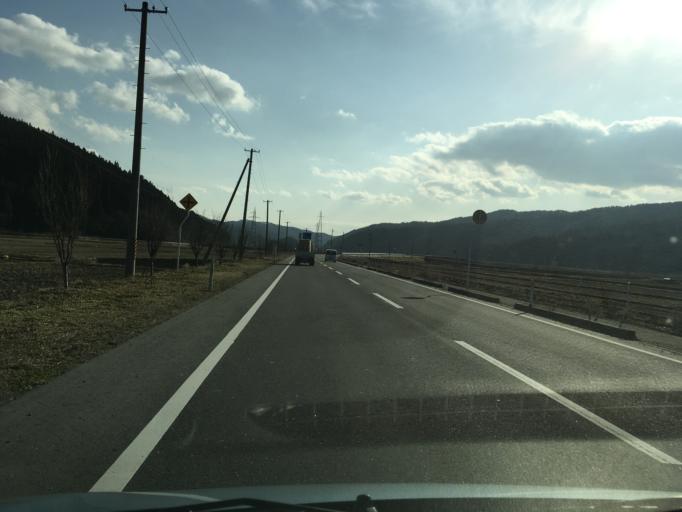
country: JP
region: Iwate
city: Ichinoseki
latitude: 38.7632
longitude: 141.3307
